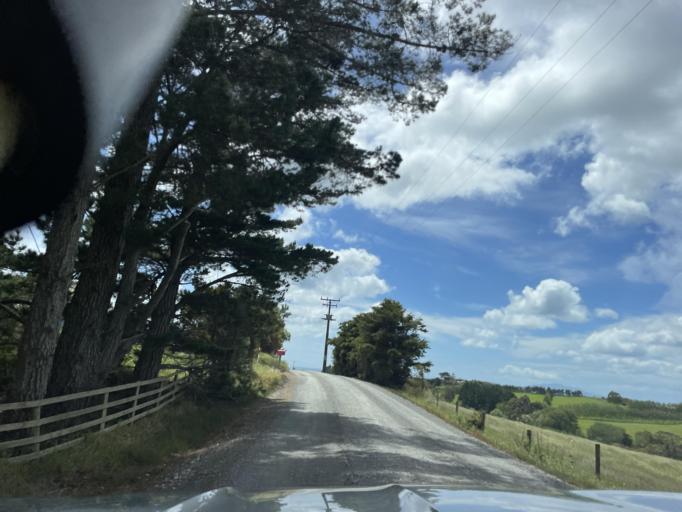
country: NZ
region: Auckland
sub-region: Auckland
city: Wellsford
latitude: -36.1726
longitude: 174.5771
